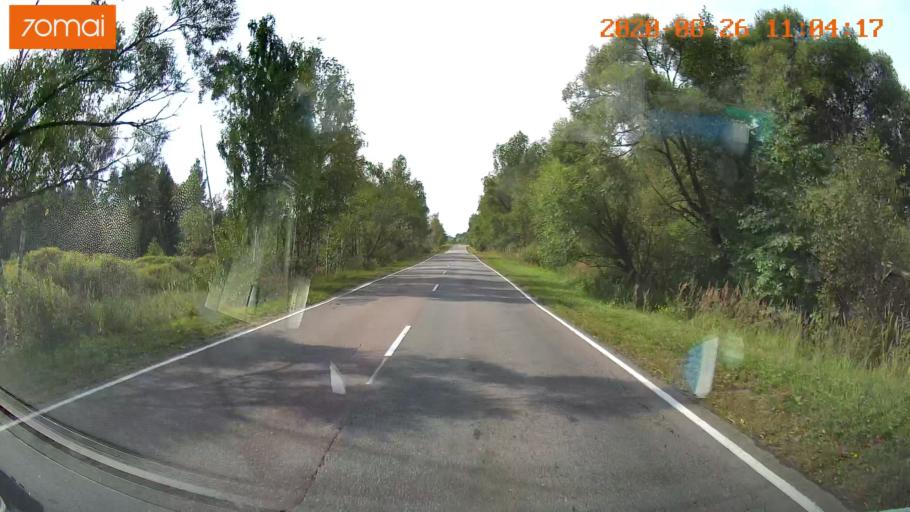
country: RU
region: Rjazan
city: Izhevskoye
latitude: 54.5314
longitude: 41.1979
